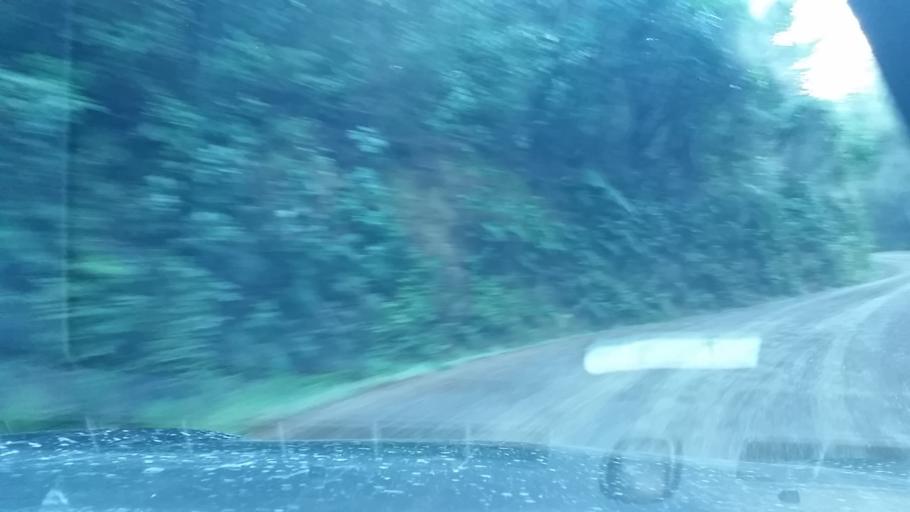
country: NZ
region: Marlborough
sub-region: Marlborough District
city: Picton
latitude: -41.1369
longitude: 174.0554
